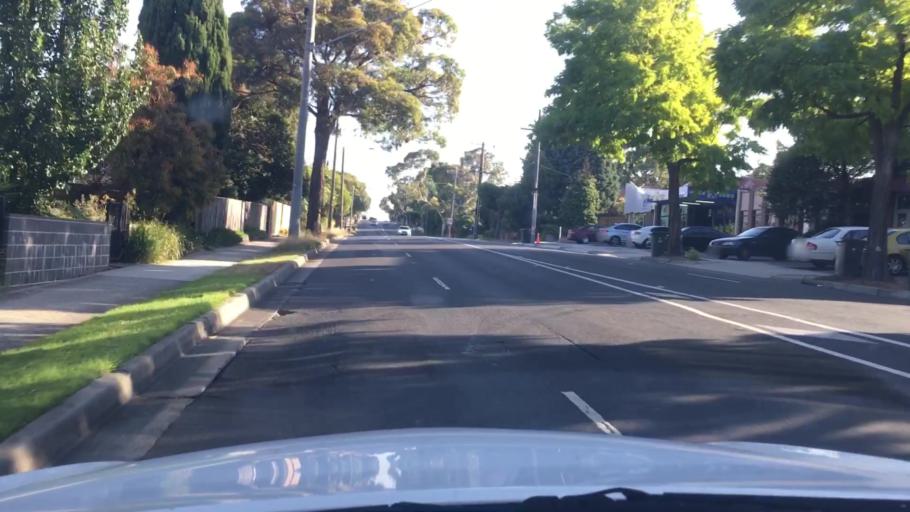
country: AU
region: Victoria
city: Burwood East
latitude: -37.8774
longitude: 145.1475
